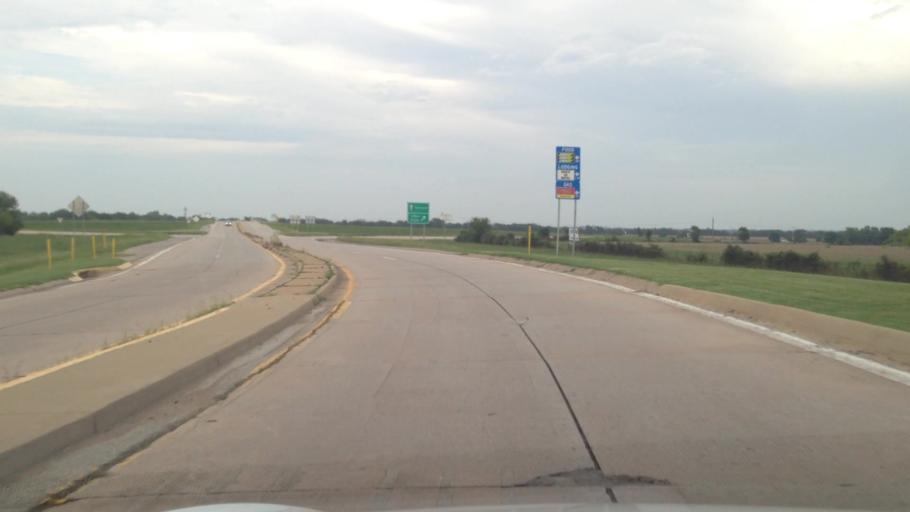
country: US
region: Oklahoma
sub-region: Ottawa County
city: Afton
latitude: 36.7185
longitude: -94.9327
